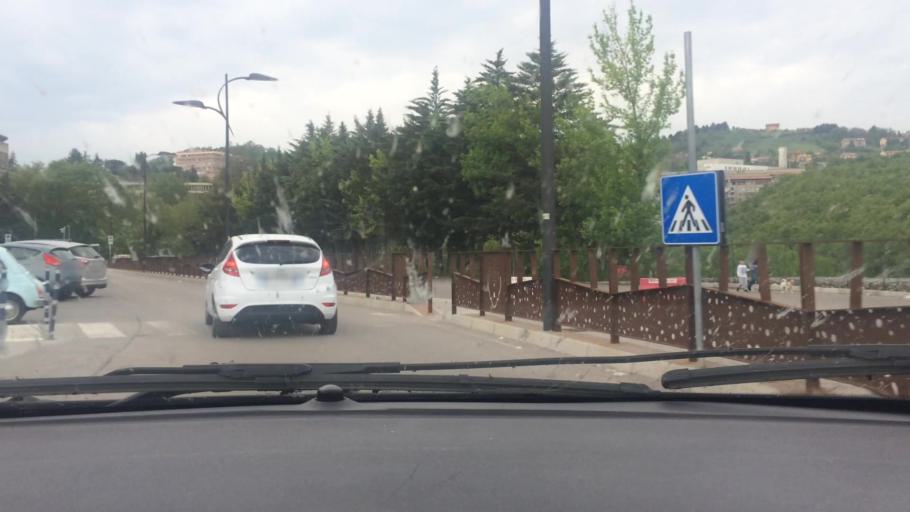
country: IT
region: Basilicate
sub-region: Provincia di Potenza
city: Potenza
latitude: 40.6530
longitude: 15.8069
